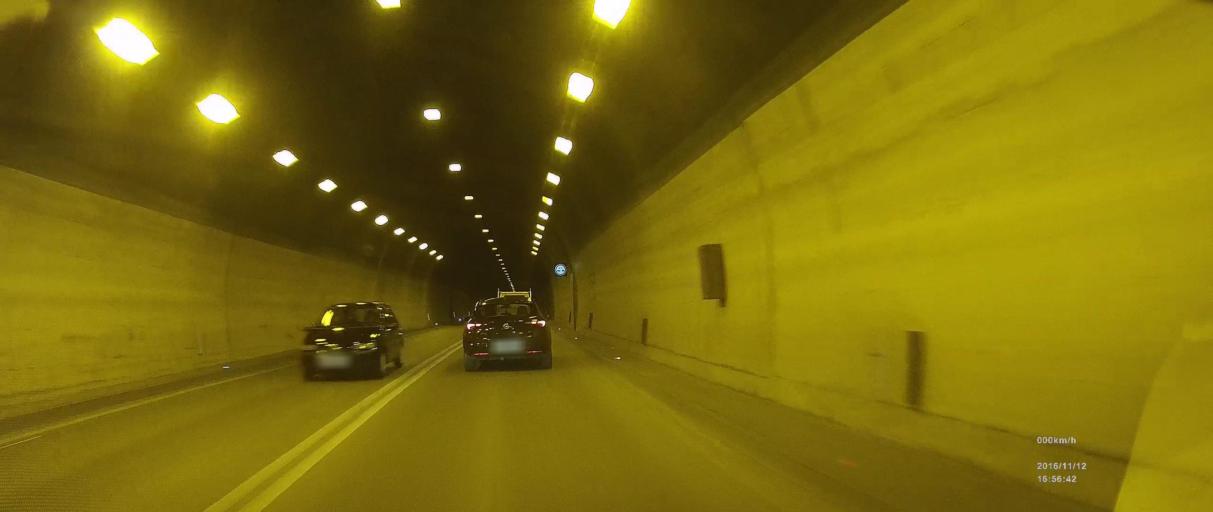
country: HR
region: Splitsko-Dalmatinska
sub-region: Grad Split
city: Split
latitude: 43.5056
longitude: 16.4238
